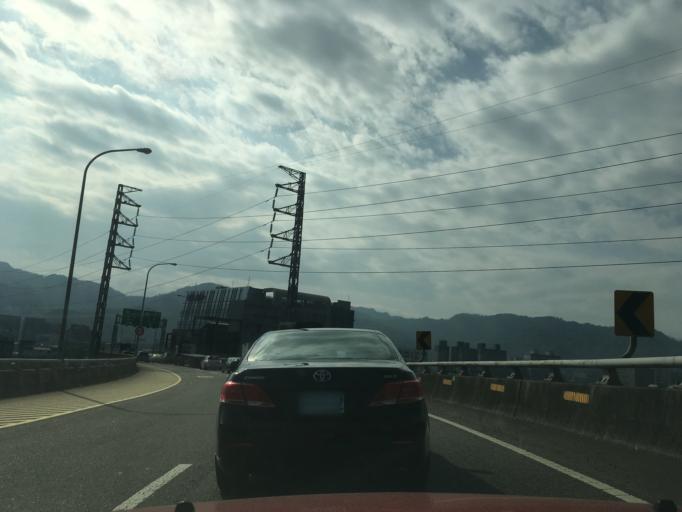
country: TW
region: Taipei
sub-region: Taipei
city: Banqiao
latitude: 24.9726
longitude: 121.4323
